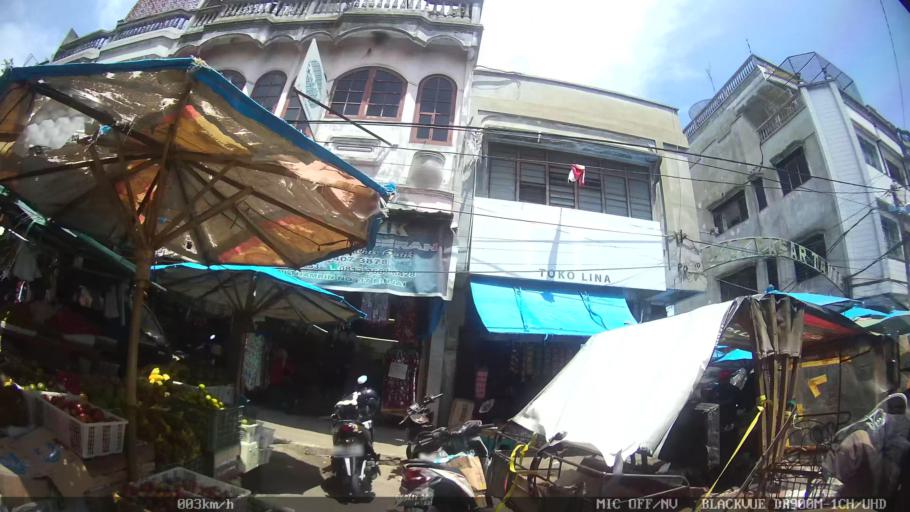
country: ID
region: North Sumatra
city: Binjai
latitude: 3.6092
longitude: 98.4894
